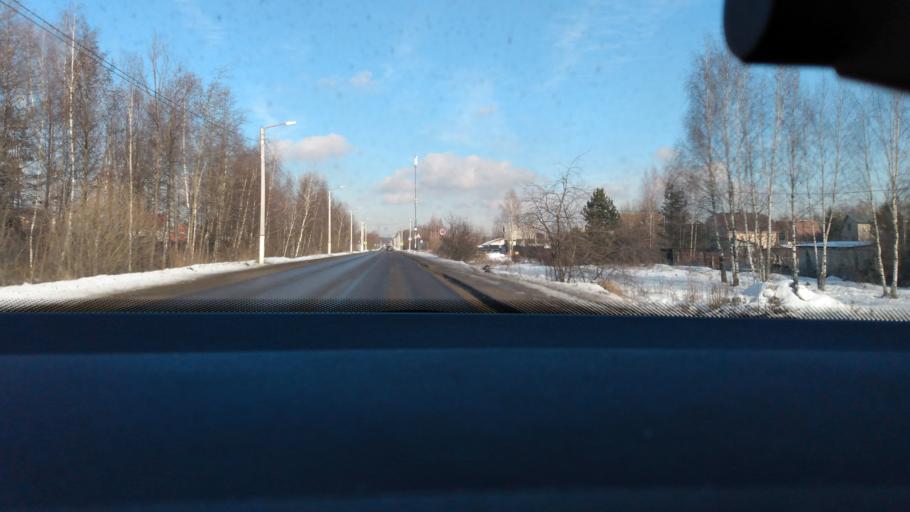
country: RU
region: Moskovskaya
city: Kratovo
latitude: 55.6233
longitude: 38.1567
